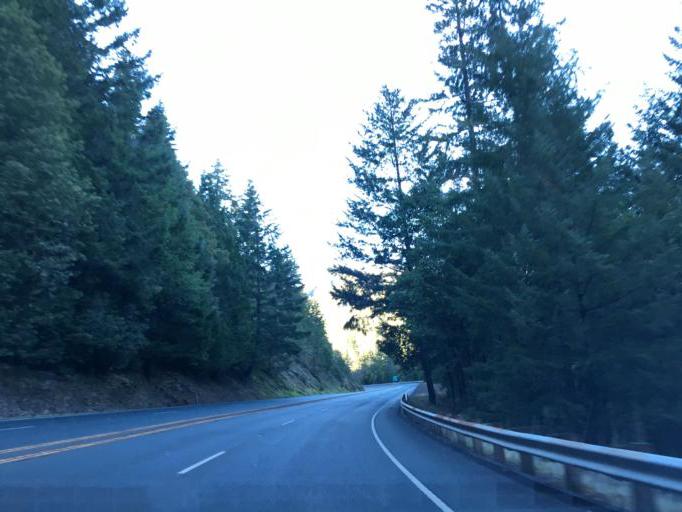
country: US
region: California
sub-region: Mendocino County
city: Laytonville
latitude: 39.8281
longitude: -123.6111
